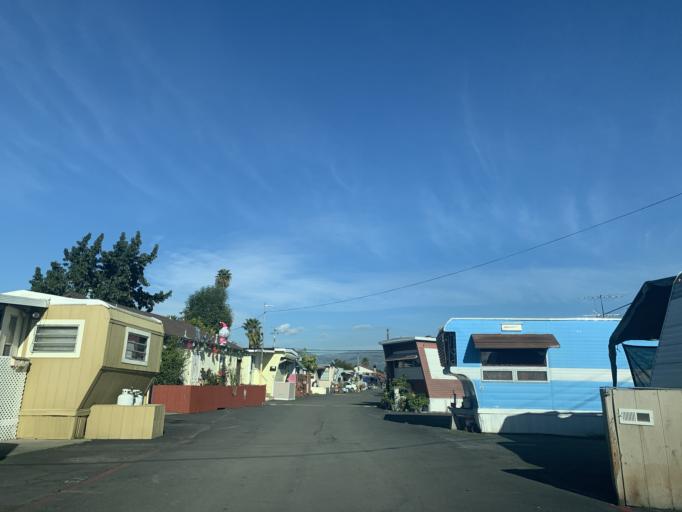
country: US
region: California
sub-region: Santa Clara County
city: San Jose
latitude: 37.3392
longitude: -121.8618
